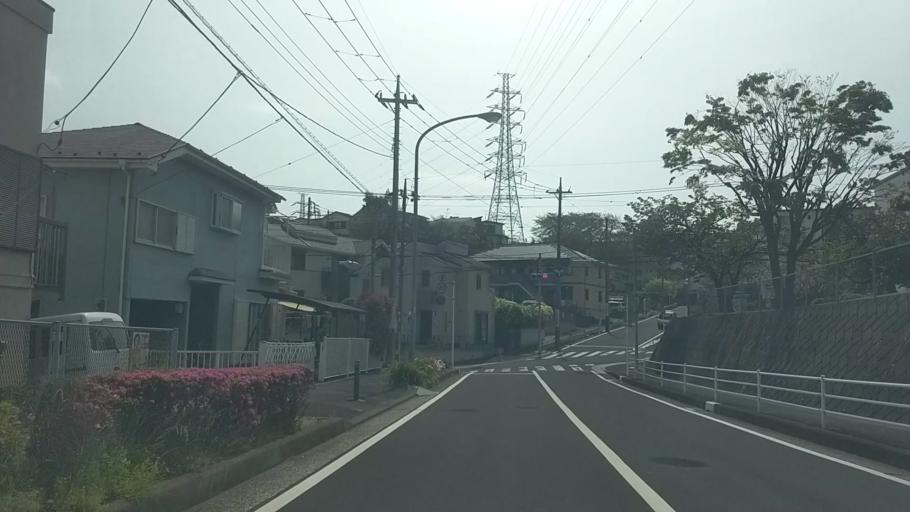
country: JP
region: Kanagawa
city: Yokohama
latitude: 35.3754
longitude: 139.6170
